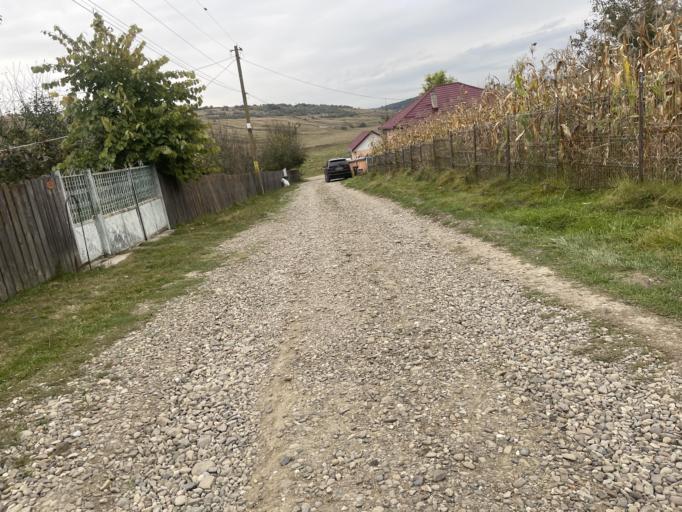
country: RO
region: Iasi
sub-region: Comuna Dumesti
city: Dumesti
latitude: 47.1727
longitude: 27.3452
